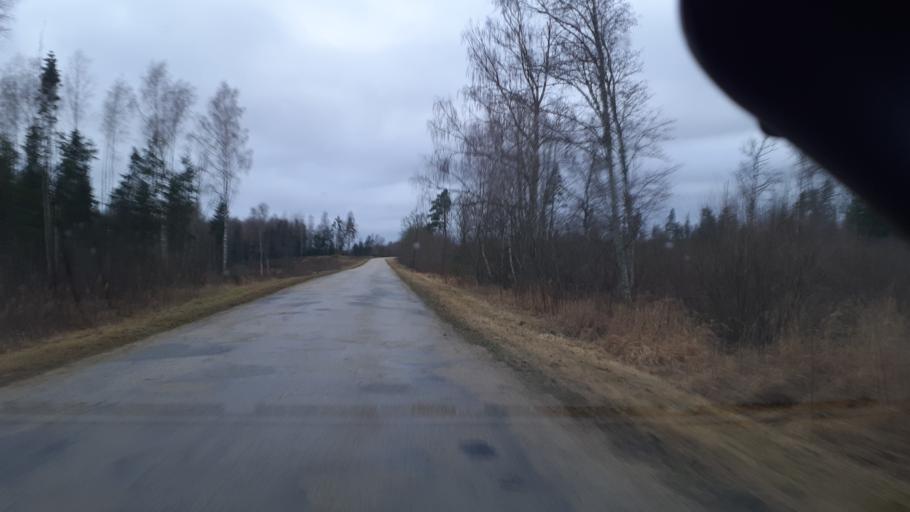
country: LV
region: Kuldigas Rajons
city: Kuldiga
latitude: 56.8724
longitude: 21.8551
